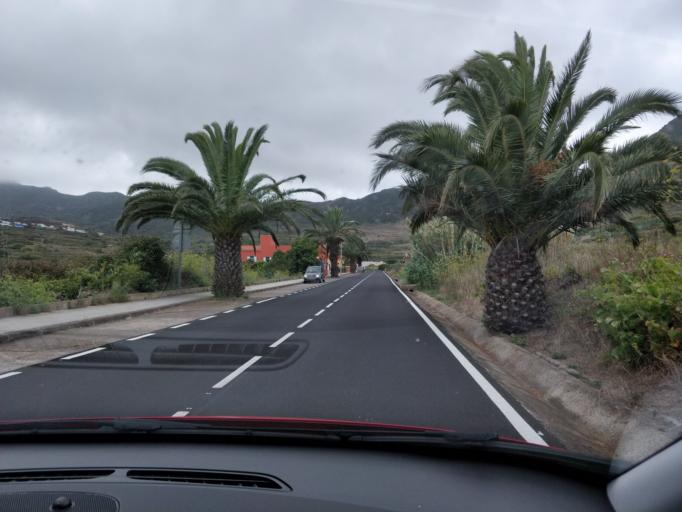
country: ES
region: Canary Islands
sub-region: Provincia de Santa Cruz de Tenerife
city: Tanque
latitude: 28.3380
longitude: -16.8517
